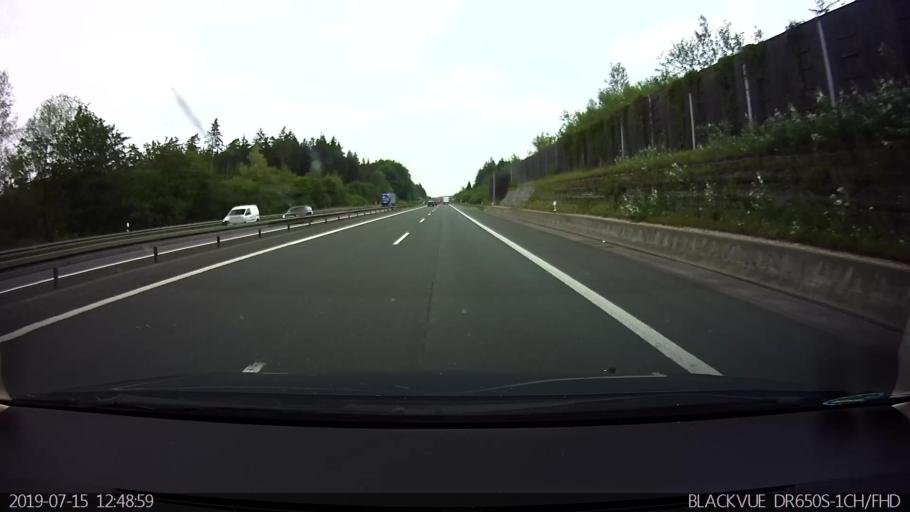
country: DE
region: Saxony
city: Waldkirchen
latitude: 50.6124
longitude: 12.4065
